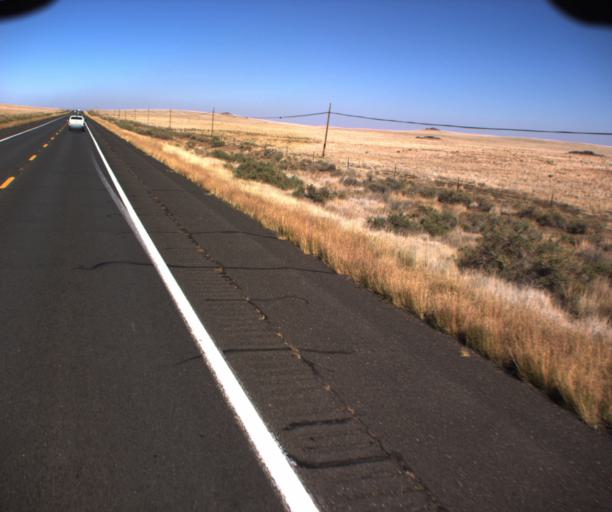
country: US
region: Arizona
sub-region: Coconino County
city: Flagstaff
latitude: 35.6005
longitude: -111.5258
